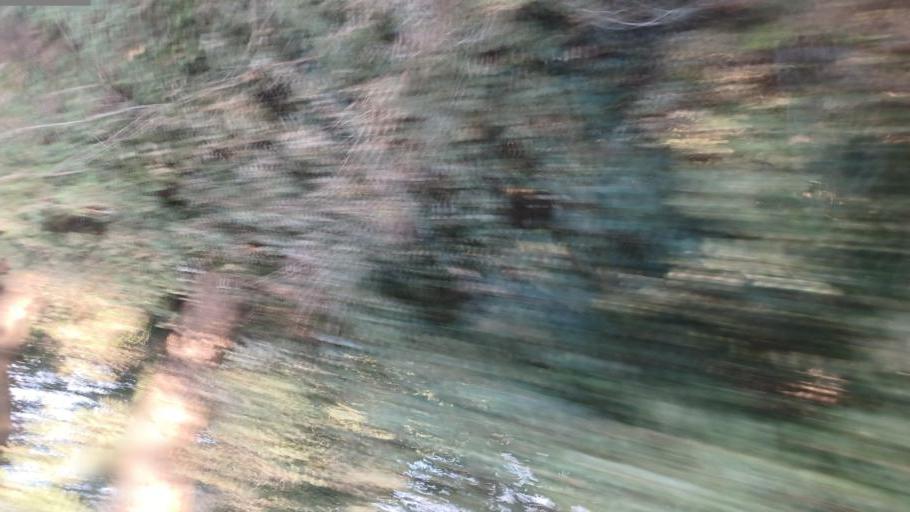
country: CY
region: Pafos
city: Tala
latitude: 34.8952
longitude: 32.4863
